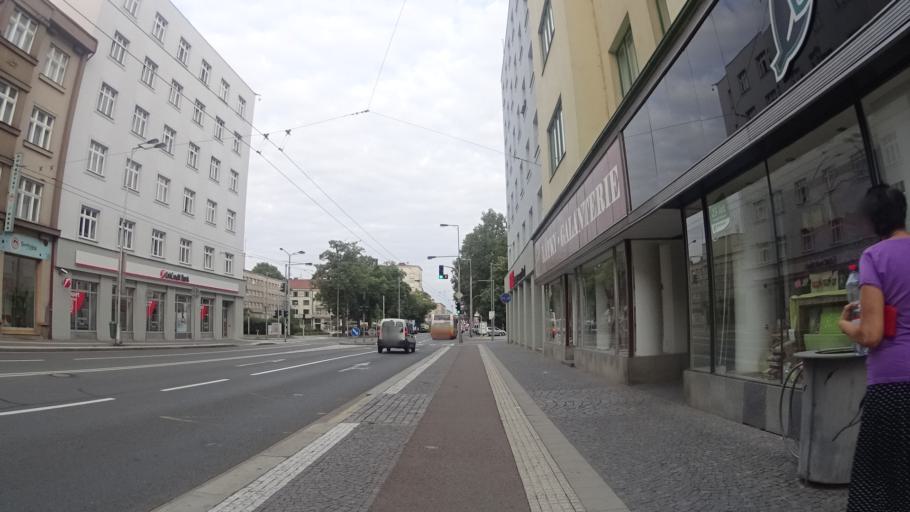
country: CZ
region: Kralovehradecky
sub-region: Okres Hradec Kralove
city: Hradec Kralove
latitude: 50.2106
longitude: 15.8240
